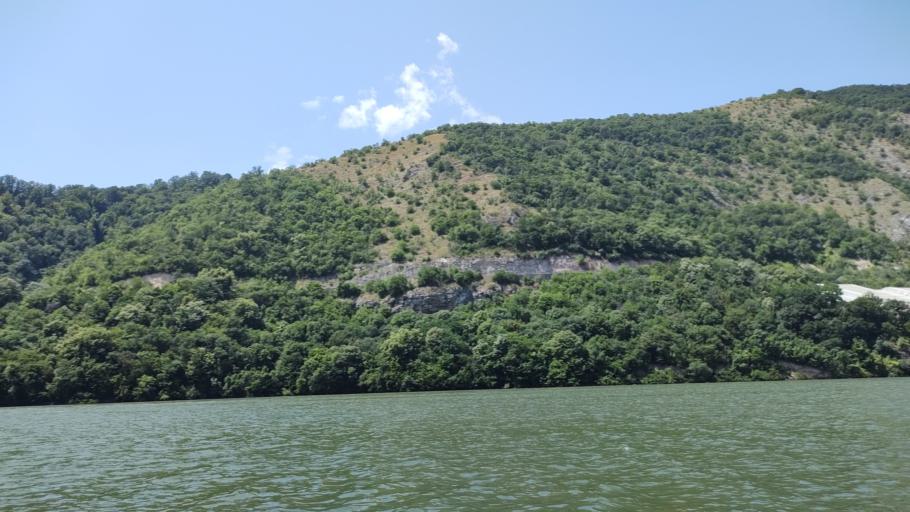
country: RO
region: Mehedinti
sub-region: Comuna Svinita
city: Svinita
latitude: 44.5553
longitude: 22.0304
